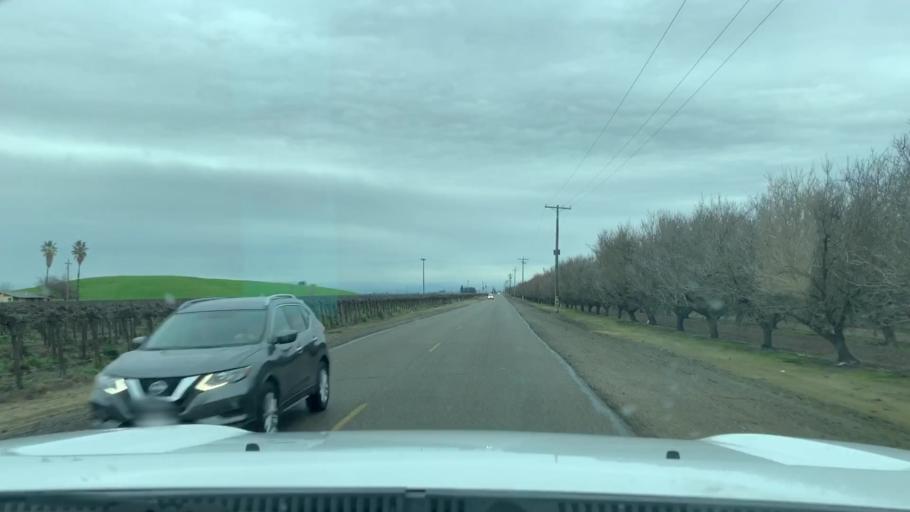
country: US
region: California
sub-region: Fresno County
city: Caruthers
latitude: 36.5473
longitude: -119.7502
